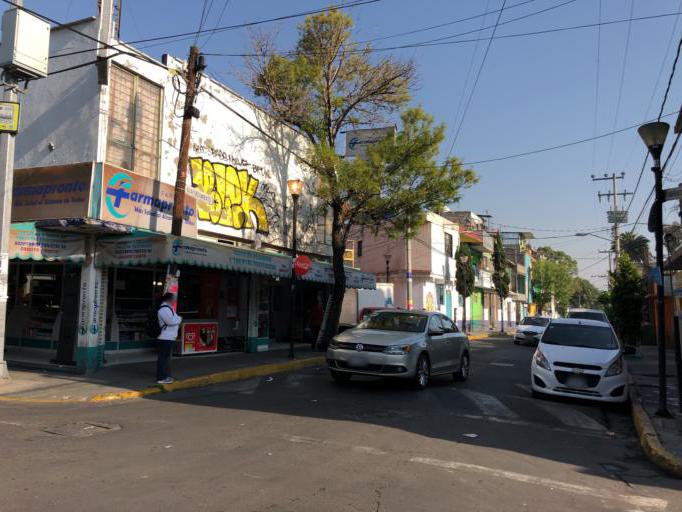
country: MX
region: Mexico City
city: Iztapalapa
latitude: 19.3617
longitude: -99.0911
